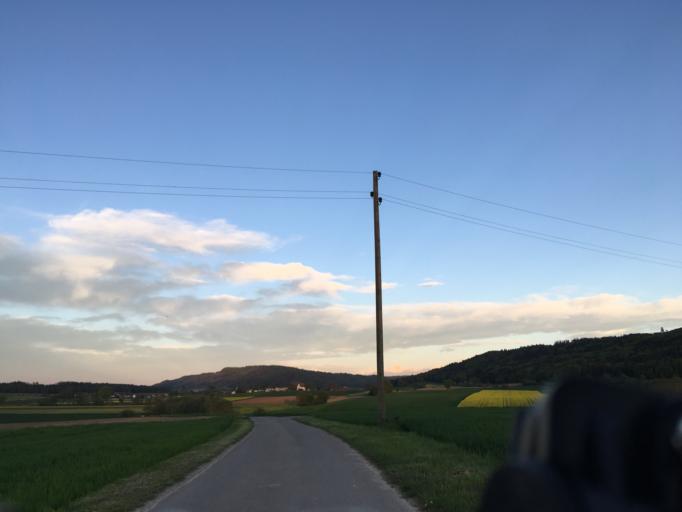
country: DE
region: Baden-Wuerttemberg
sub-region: Freiburg Region
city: Gottmadingen
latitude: 47.7209
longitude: 8.7634
